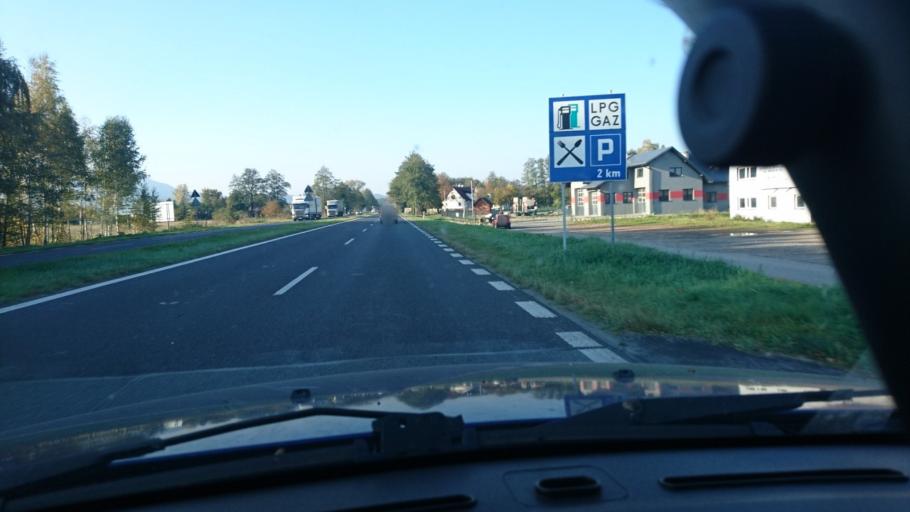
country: PL
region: Silesian Voivodeship
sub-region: Powiat cieszynski
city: Ustron
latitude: 49.7570
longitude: 18.8023
